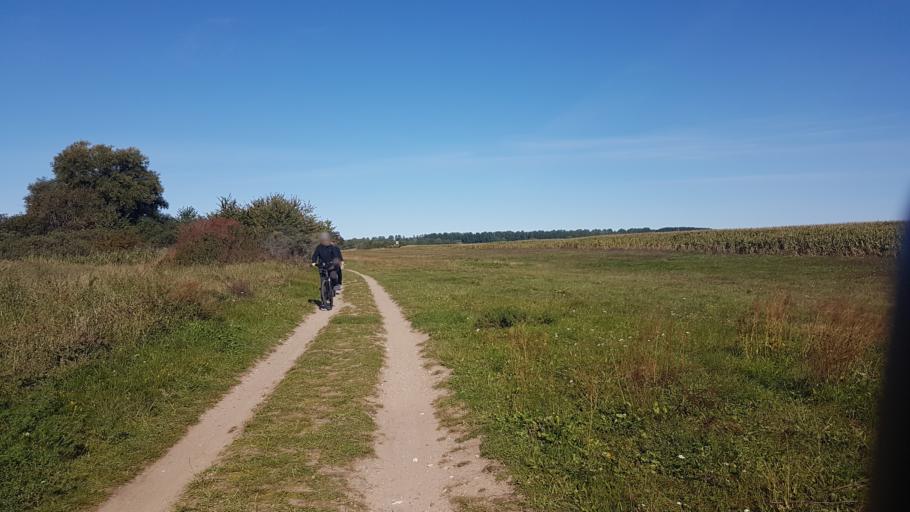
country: DE
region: Mecklenburg-Vorpommern
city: Glowe
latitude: 54.5504
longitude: 13.5023
